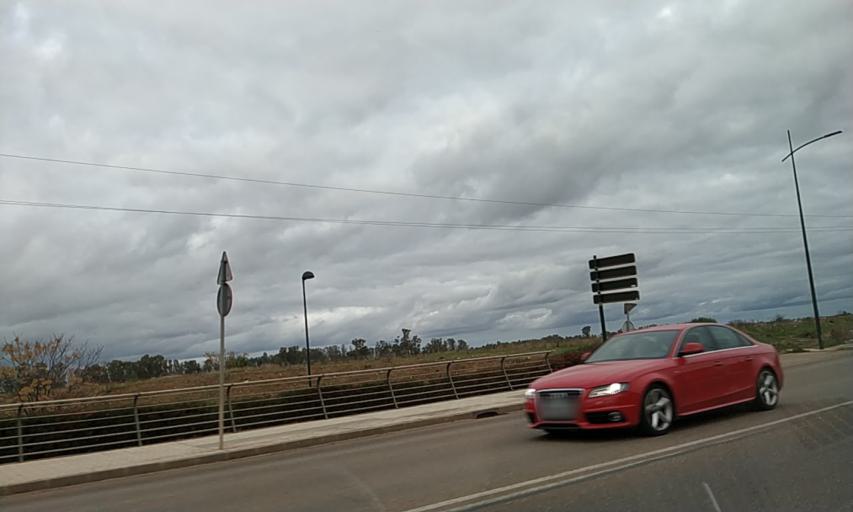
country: ES
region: Extremadura
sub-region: Provincia de Badajoz
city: Badajoz
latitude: 38.8825
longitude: -6.9632
